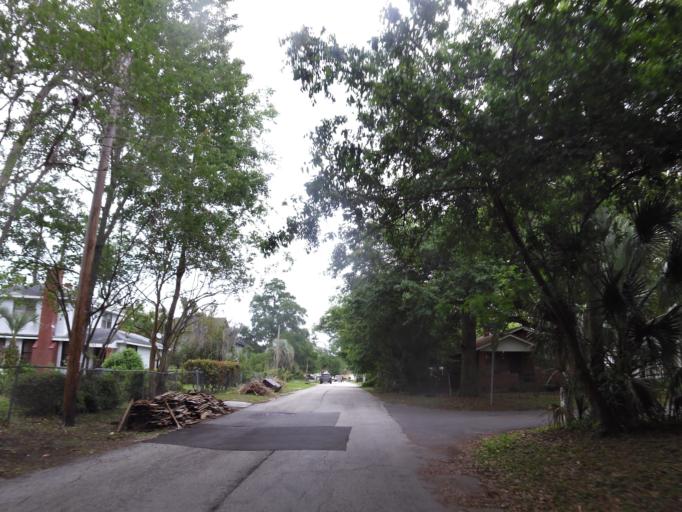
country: US
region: Florida
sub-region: Duval County
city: Jacksonville
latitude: 30.2927
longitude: -81.6426
